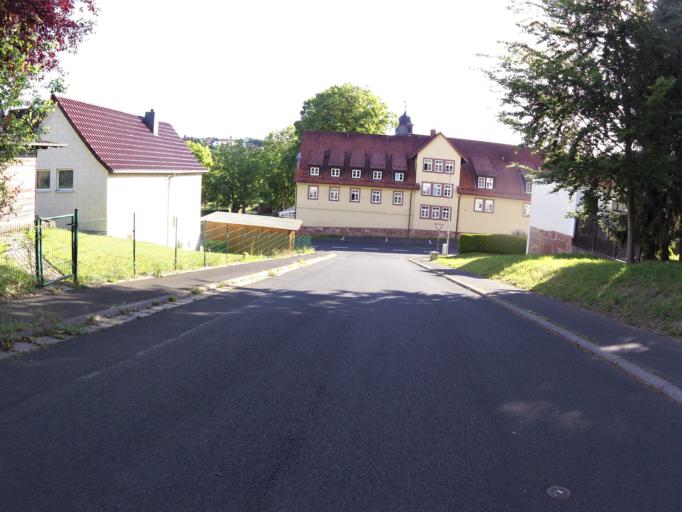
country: DE
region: Hesse
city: Philippsthal
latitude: 50.8419
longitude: 10.0069
